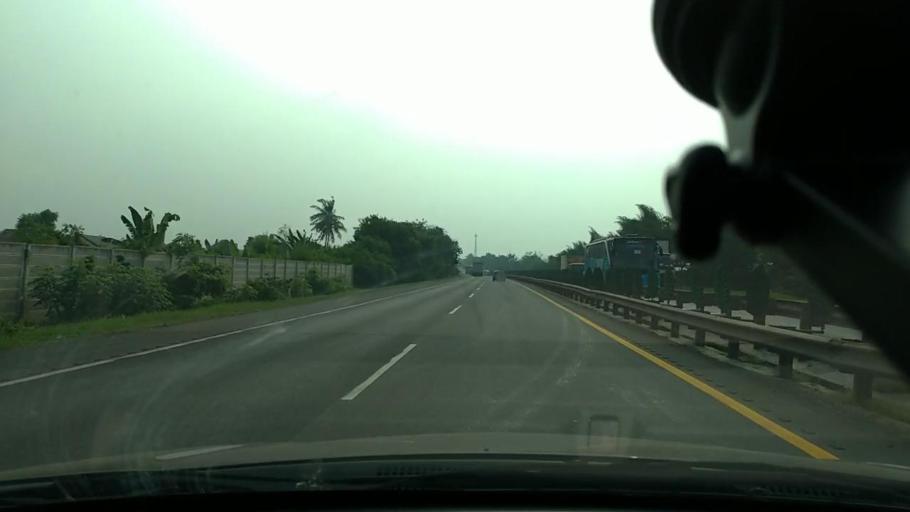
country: ID
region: Banten
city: Serang
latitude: -6.0950
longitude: 106.1635
